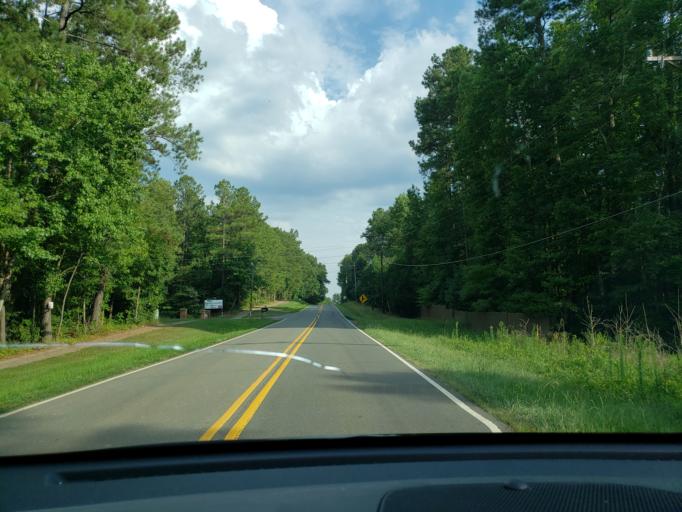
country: US
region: North Carolina
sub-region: Orange County
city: Chapel Hill
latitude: 35.9037
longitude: -78.9823
